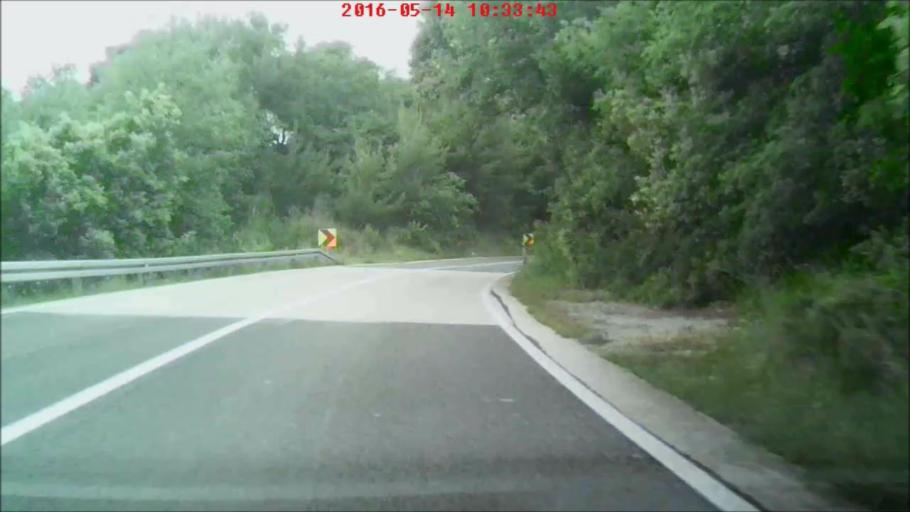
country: HR
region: Dubrovacko-Neretvanska
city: Podgora
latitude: 42.7760
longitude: 17.8878
